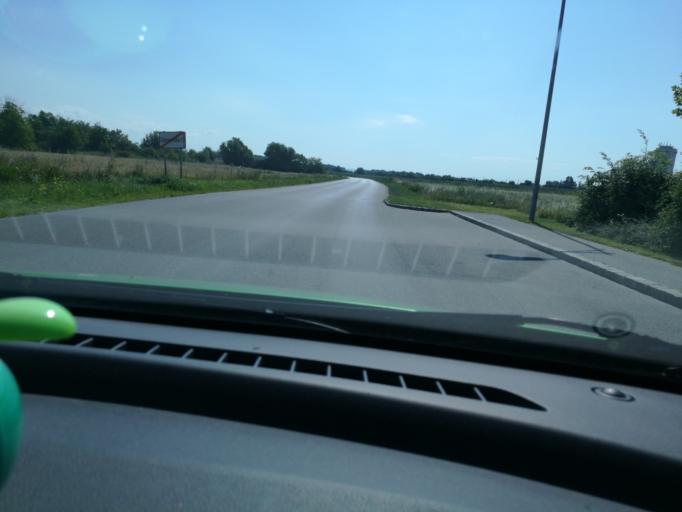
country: AT
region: Lower Austria
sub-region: Politischer Bezirk Ganserndorf
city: Ganserndorf
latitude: 48.3462
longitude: 16.7294
